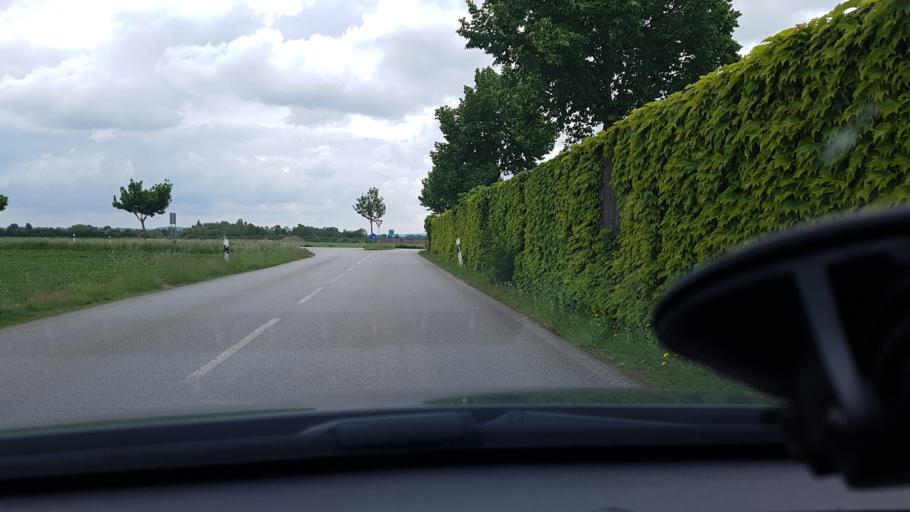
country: DE
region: Bavaria
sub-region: Lower Bavaria
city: Pocking
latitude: 48.4060
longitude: 13.3381
